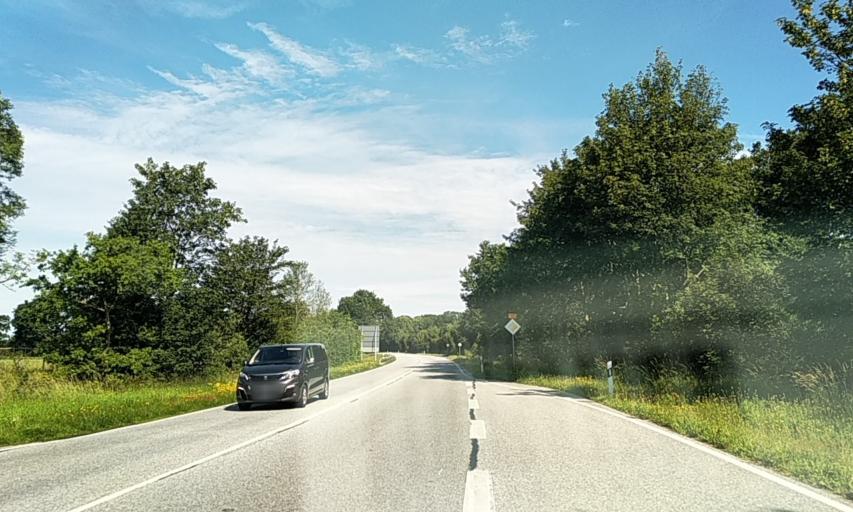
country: DE
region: Schleswig-Holstein
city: Fockbek
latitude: 54.3324
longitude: 9.6202
